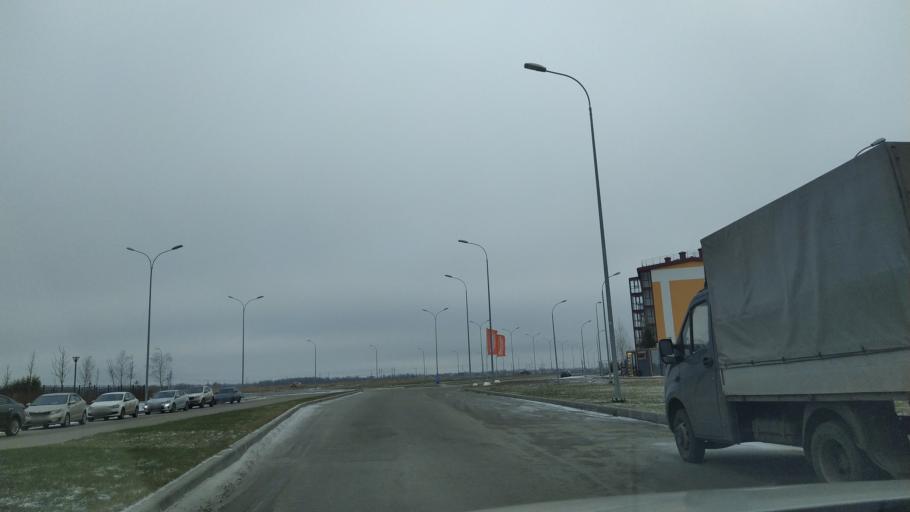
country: RU
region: St.-Petersburg
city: Aleksandrovskaya
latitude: 59.7555
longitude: 30.3659
